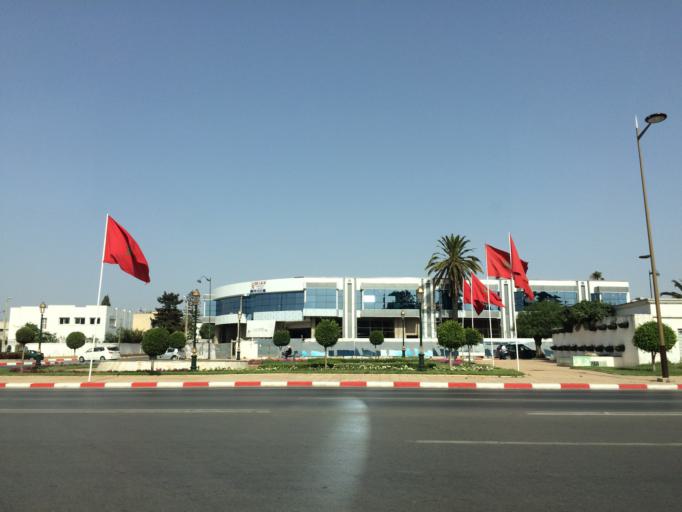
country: MA
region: Rabat-Sale-Zemmour-Zaer
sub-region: Rabat
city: Rabat
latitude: 33.9886
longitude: -6.8283
